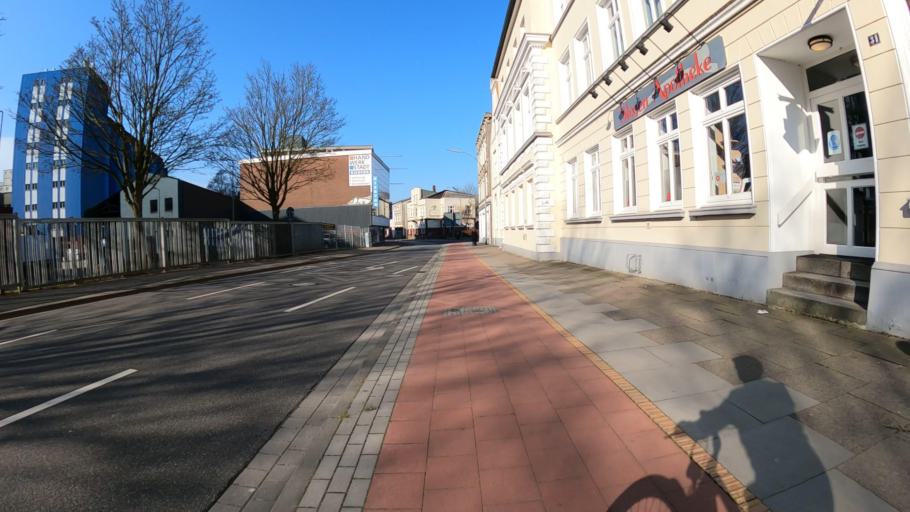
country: DE
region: Schleswig-Holstein
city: Elmshorn
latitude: 53.7501
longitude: 9.6561
